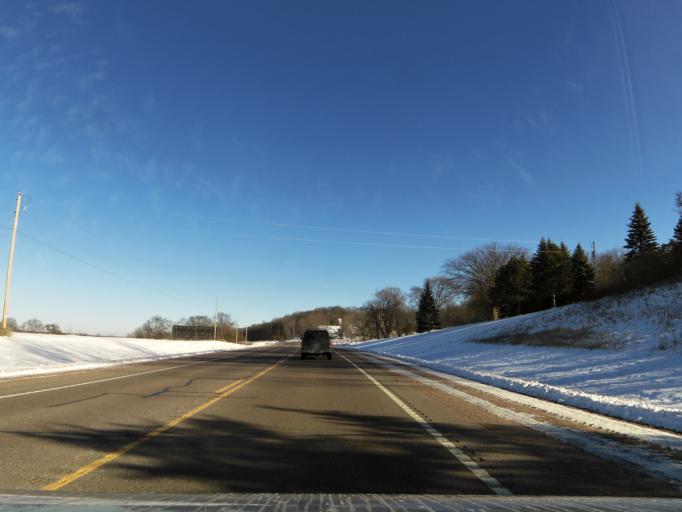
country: US
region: Wisconsin
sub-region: Columbia County
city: Lake Wisconsin
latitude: 43.5034
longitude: -89.6122
